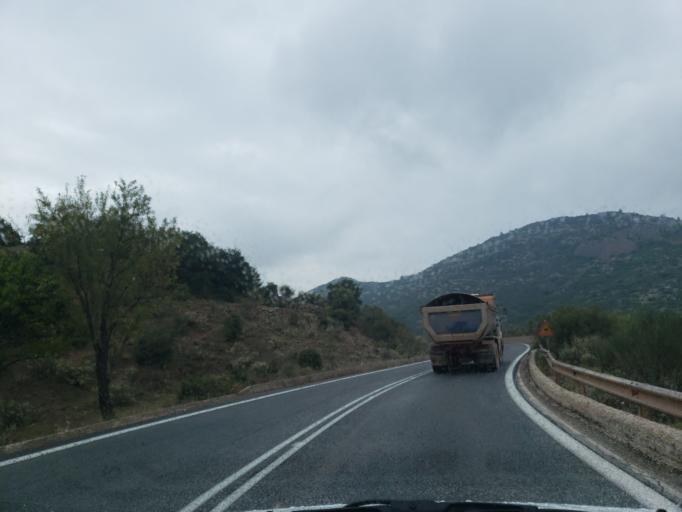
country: GR
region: Central Greece
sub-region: Nomos Fokidos
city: Amfissa
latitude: 38.5756
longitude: 22.3942
